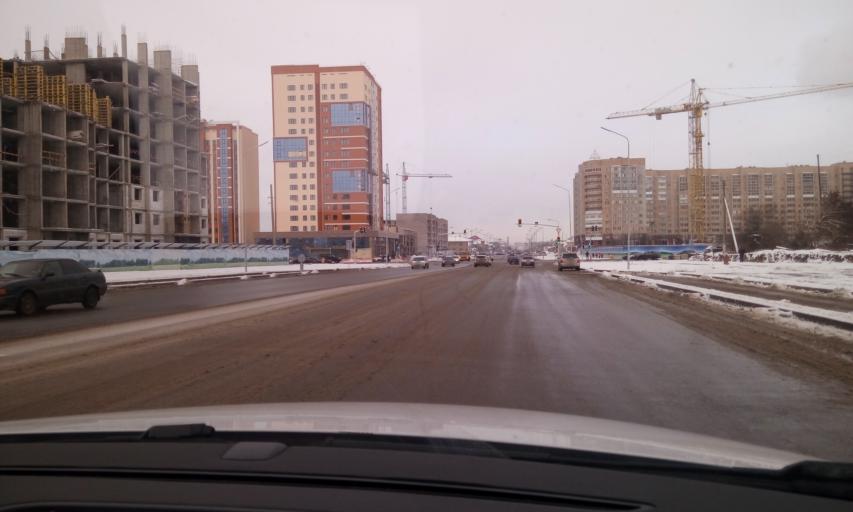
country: KZ
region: Astana Qalasy
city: Astana
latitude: 51.1279
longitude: 71.4982
